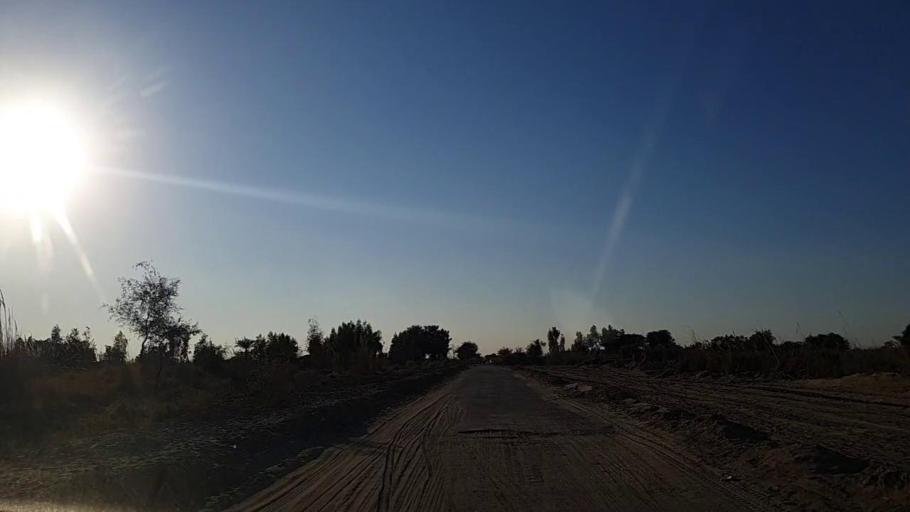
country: PK
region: Sindh
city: Khadro
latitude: 26.2791
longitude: 68.8626
